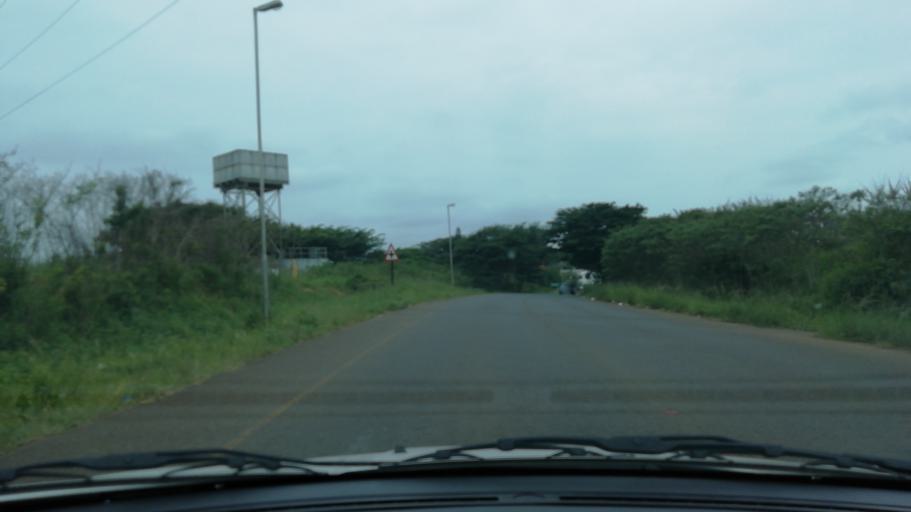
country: ZA
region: KwaZulu-Natal
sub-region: uThungulu District Municipality
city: Empangeni
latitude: -28.7360
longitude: 31.8912
